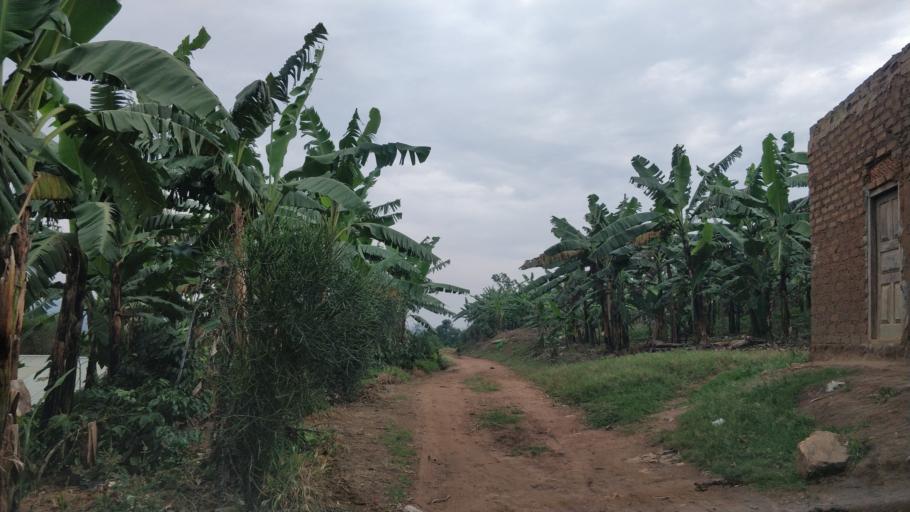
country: UG
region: Western Region
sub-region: Sheema District
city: Kibingo
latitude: -0.6986
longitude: 30.3918
